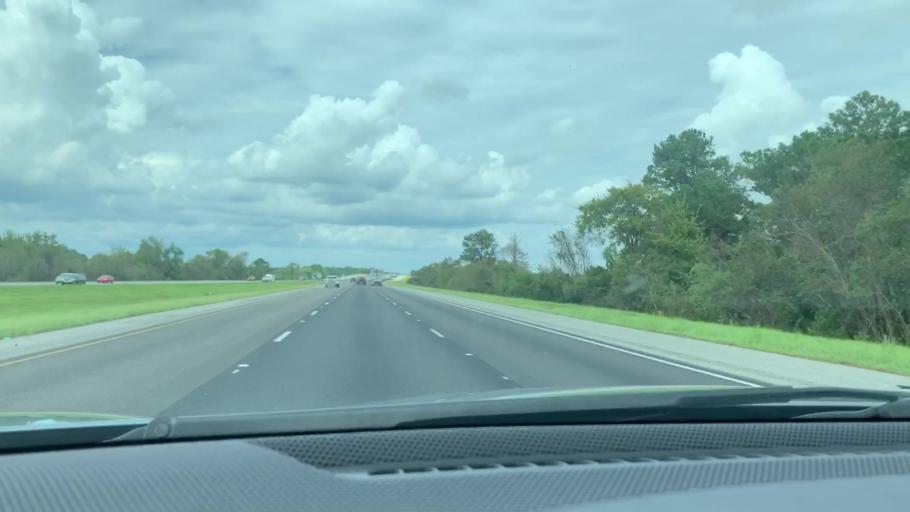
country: US
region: Georgia
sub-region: Liberty County
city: Midway
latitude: 31.7279
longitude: -81.3882
